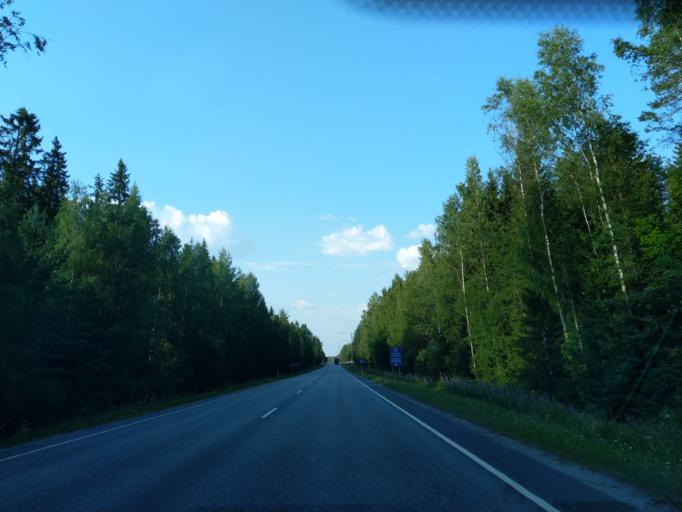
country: FI
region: Satakunta
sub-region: Pori
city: Pomarkku
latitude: 61.6868
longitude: 21.9950
